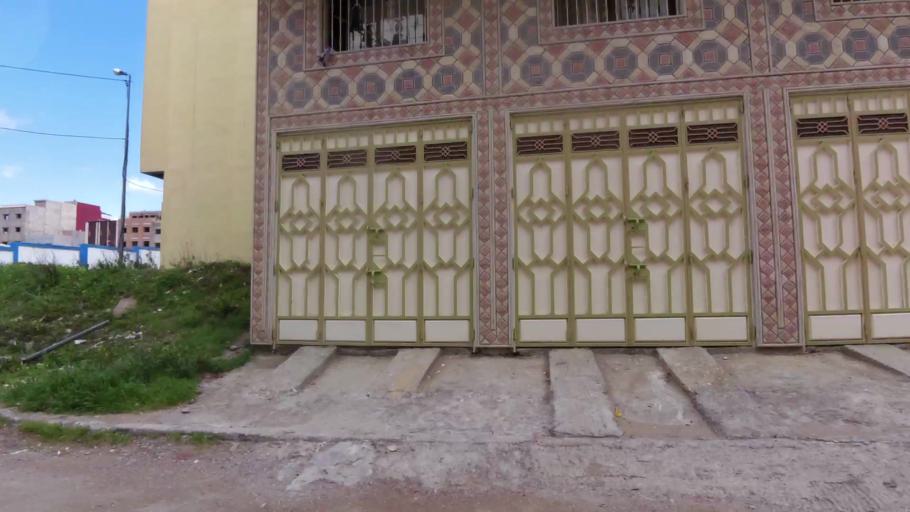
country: MA
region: Tanger-Tetouan
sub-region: Tanger-Assilah
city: Tangier
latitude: 35.7598
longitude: -5.8511
